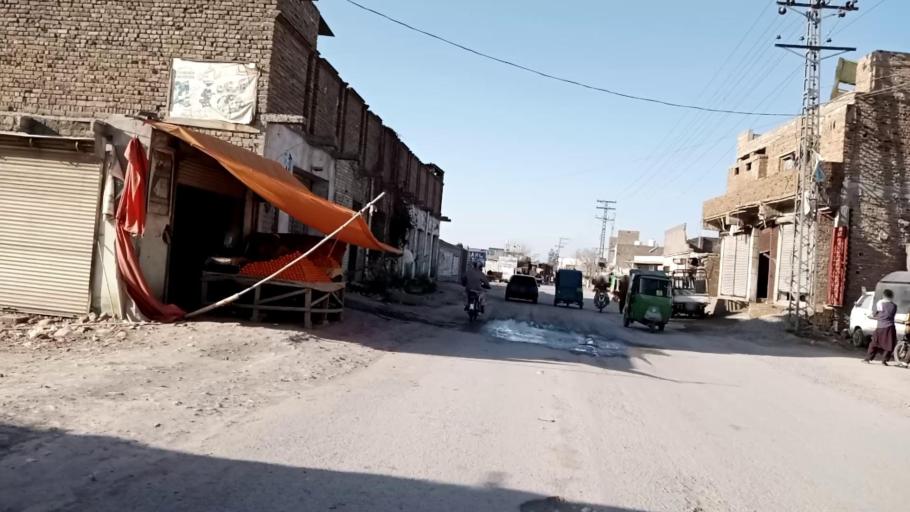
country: PK
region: Khyber Pakhtunkhwa
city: Peshawar
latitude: 34.0597
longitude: 71.5399
